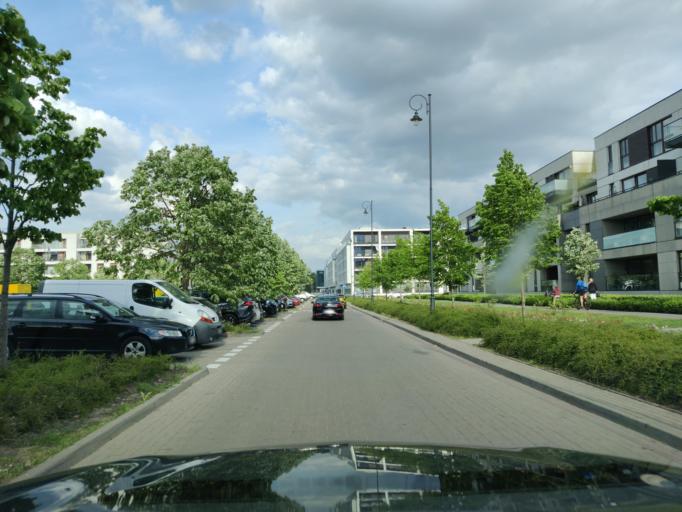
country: PL
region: Masovian Voivodeship
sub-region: Warszawa
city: Wilanow
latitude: 52.1647
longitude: 21.0773
